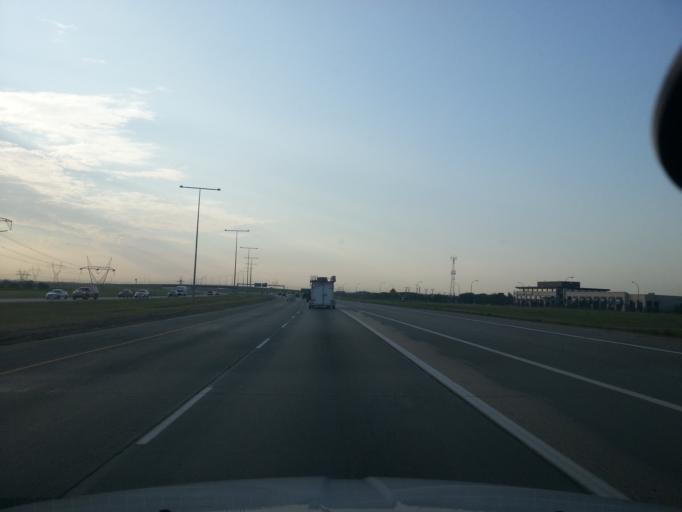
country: CA
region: Alberta
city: Devon
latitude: 53.4357
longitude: -113.5934
